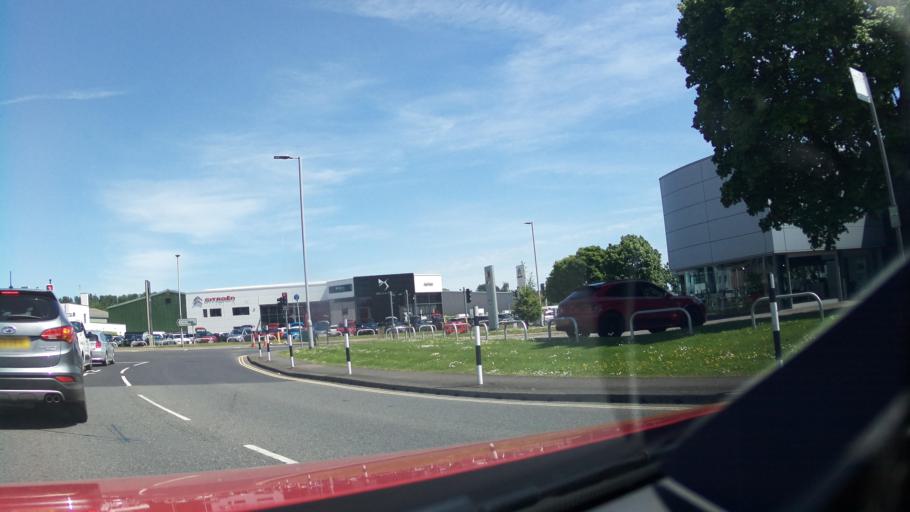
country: GB
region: England
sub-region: Devon
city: Exeter
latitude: 50.7009
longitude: -3.5251
